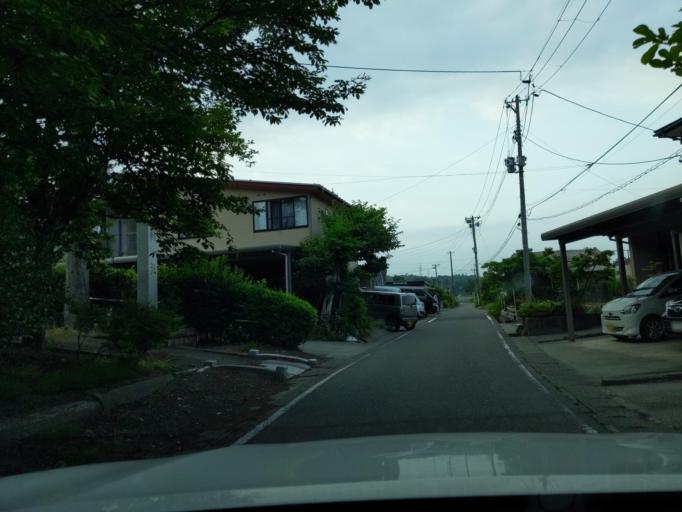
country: JP
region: Niigata
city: Kashiwazaki
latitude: 37.4008
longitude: 138.6001
